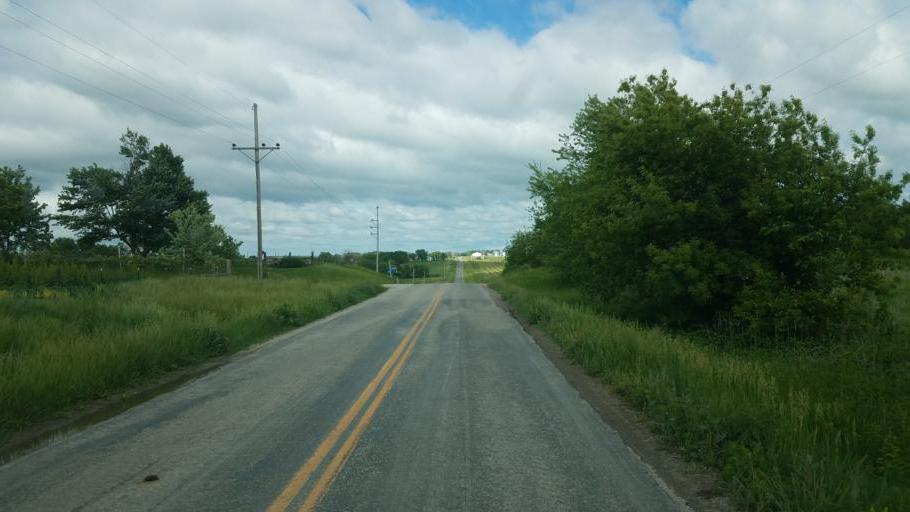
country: US
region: Missouri
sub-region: Mercer County
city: Princeton
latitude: 40.3003
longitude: -93.7070
